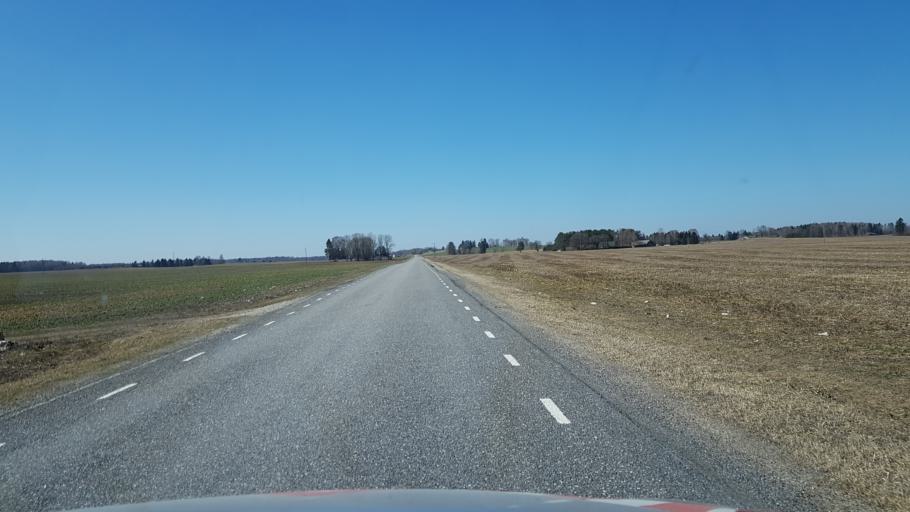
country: EE
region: Laeaene-Virumaa
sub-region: Rakke vald
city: Rakke
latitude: 59.0080
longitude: 26.1598
